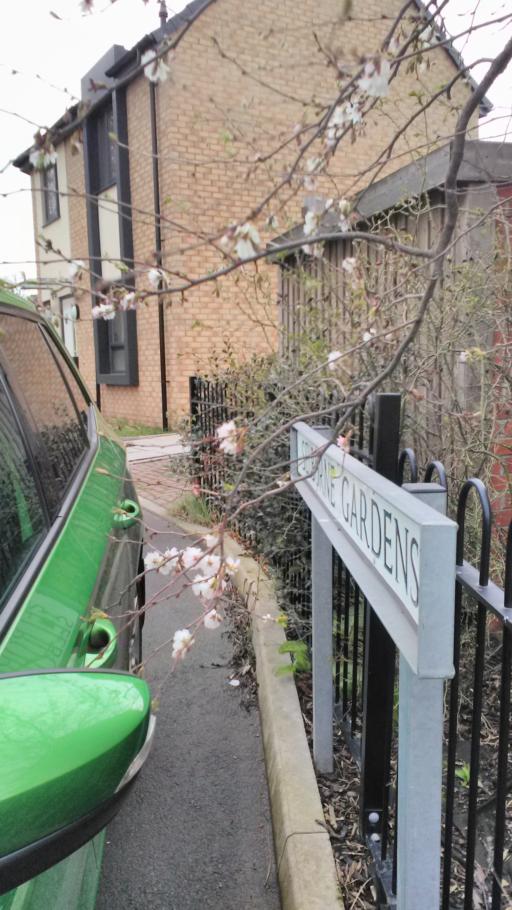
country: GB
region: England
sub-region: Nottingham
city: Nottingham
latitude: 52.9593
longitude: -1.1338
